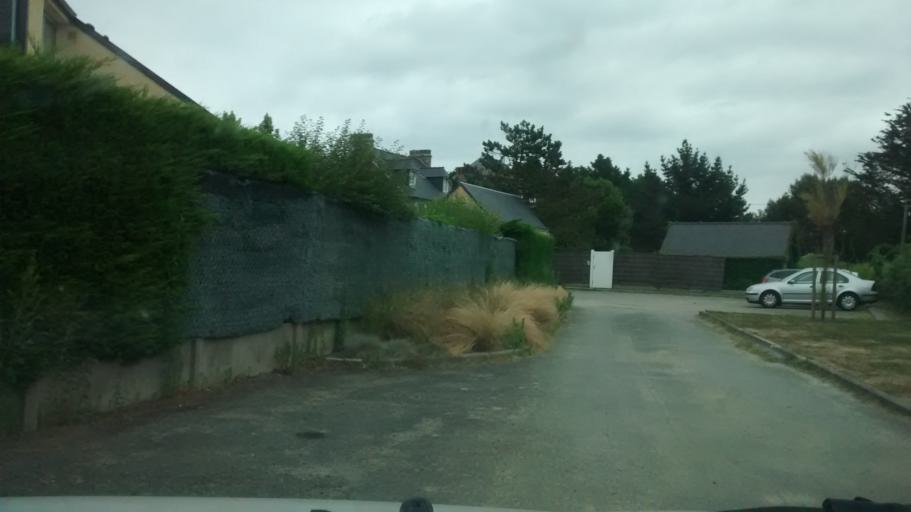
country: FR
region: Brittany
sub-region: Departement d'Ille-et-Vilaine
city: Dinard
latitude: 48.6333
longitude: -2.0864
